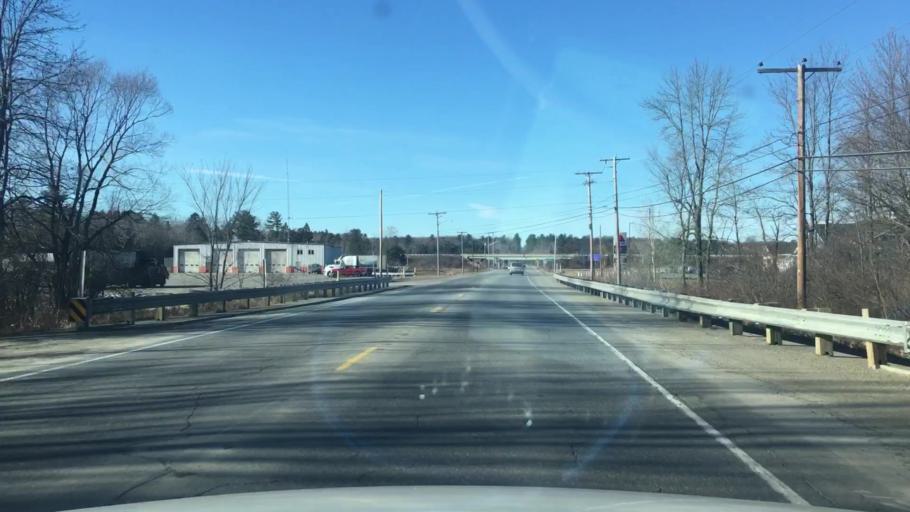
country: US
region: Maine
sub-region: Kennebec County
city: Clinton
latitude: 44.6391
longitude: -69.5223
